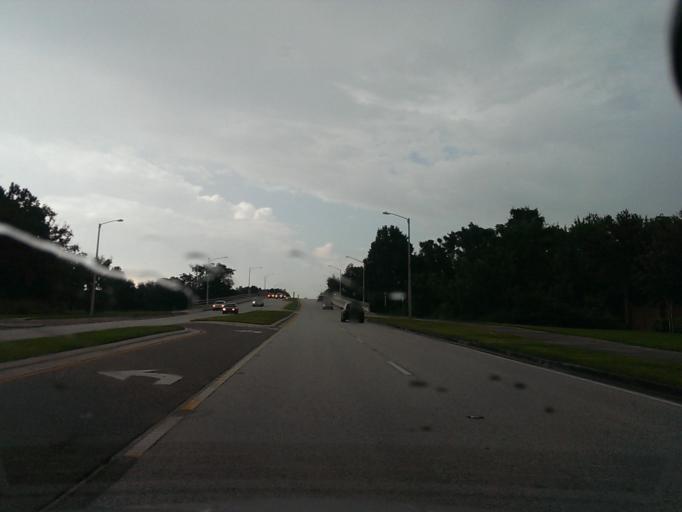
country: US
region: Florida
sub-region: Orange County
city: Winter Garden
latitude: 28.5428
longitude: -81.5834
